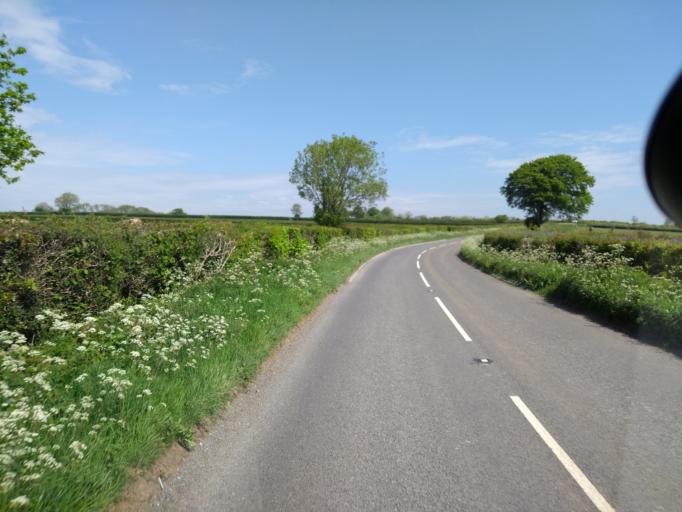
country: GB
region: England
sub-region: Somerset
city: Chard
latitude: 50.9009
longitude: -3.0079
